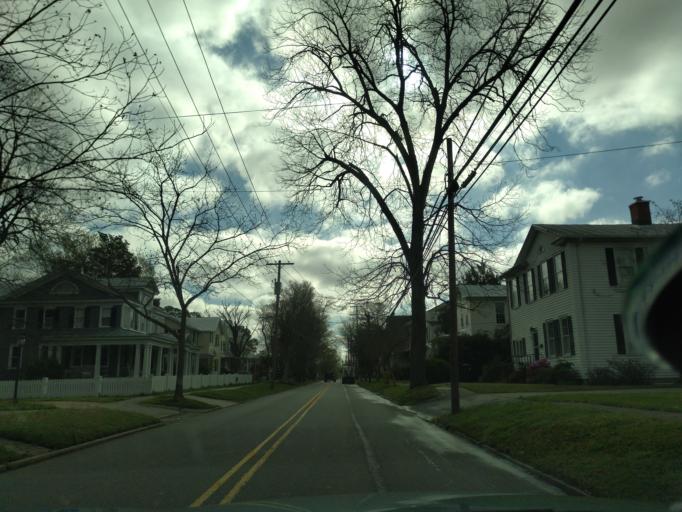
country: US
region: North Carolina
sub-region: Chowan County
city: Edenton
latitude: 36.0609
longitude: -76.6133
